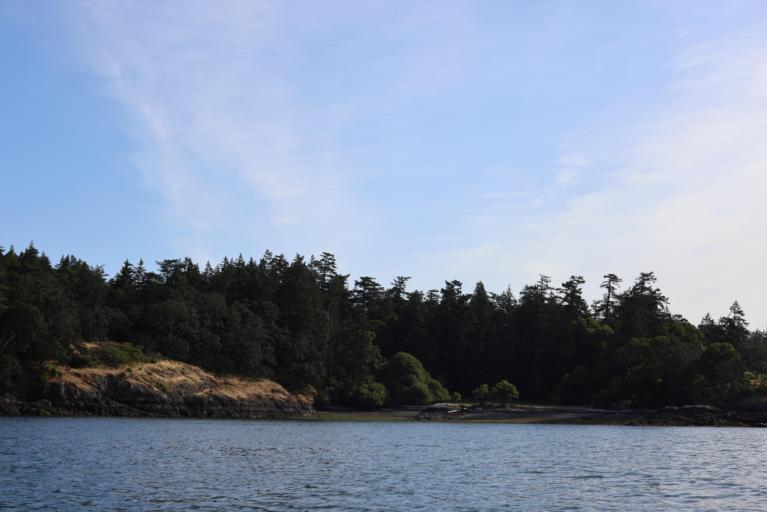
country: CA
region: British Columbia
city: Metchosin
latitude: 48.3385
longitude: -123.5489
